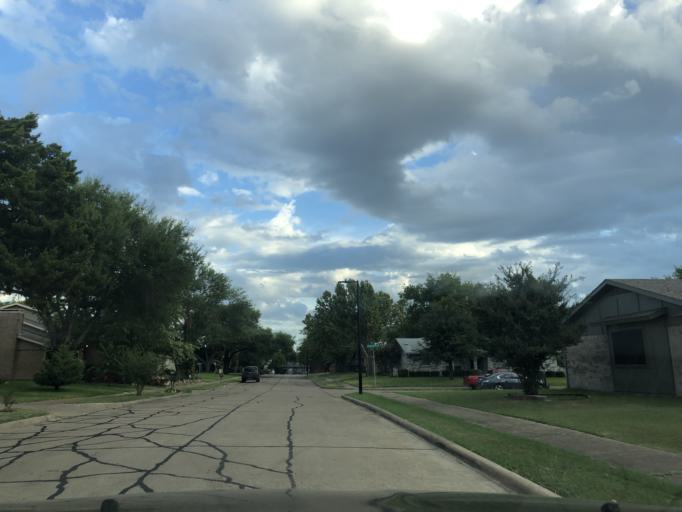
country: US
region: Texas
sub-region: Dallas County
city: Garland
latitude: 32.8732
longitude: -96.6566
